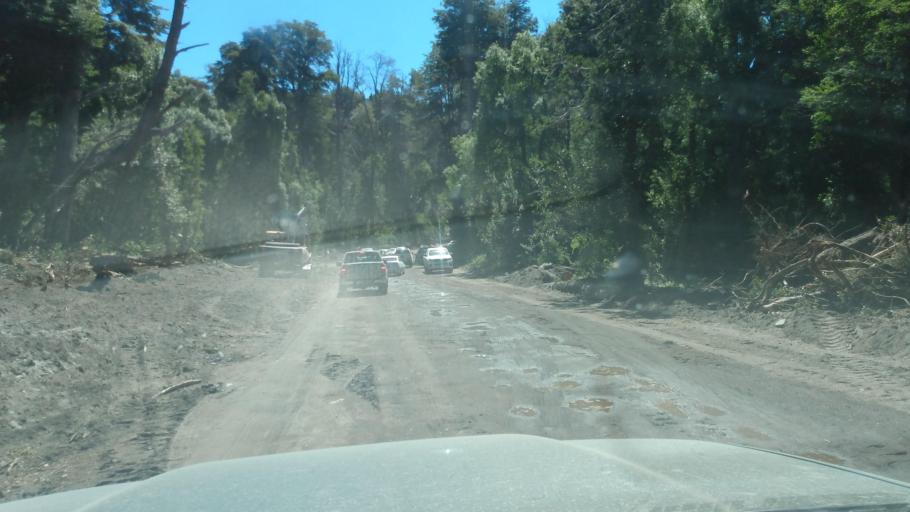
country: AR
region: Neuquen
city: Villa La Angostura
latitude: -40.6264
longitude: -71.4985
